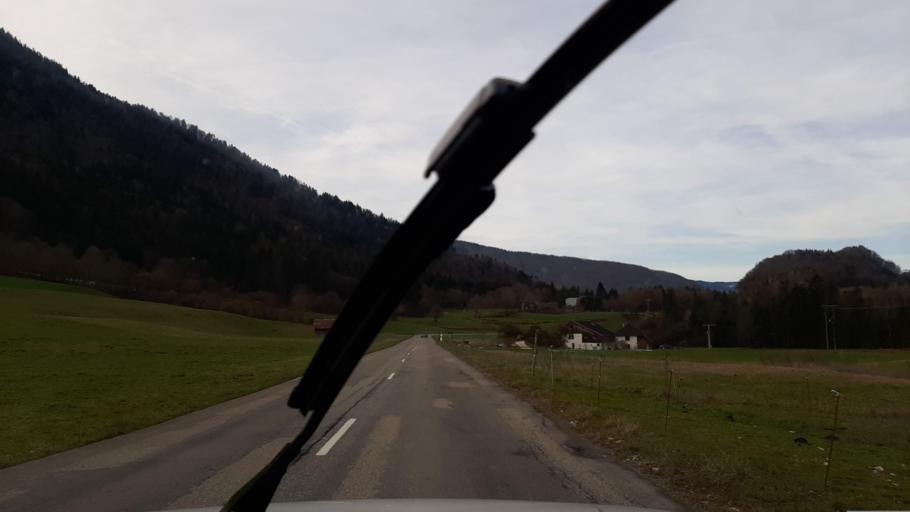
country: FR
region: Rhone-Alpes
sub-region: Departement de la Savoie
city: Gresy-sur-Isere
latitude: 45.6693
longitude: 6.1500
